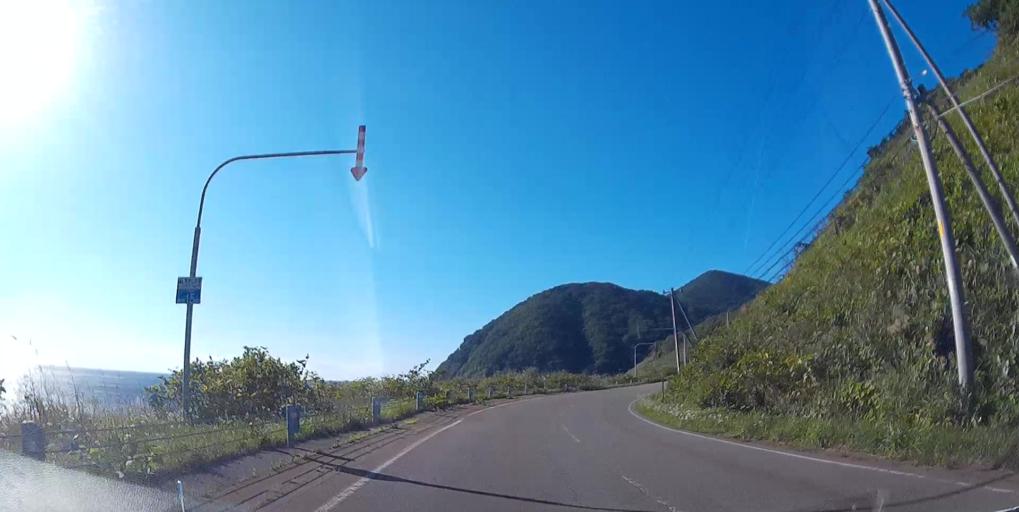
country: JP
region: Hokkaido
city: Kamiiso
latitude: 42.2461
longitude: 139.7870
